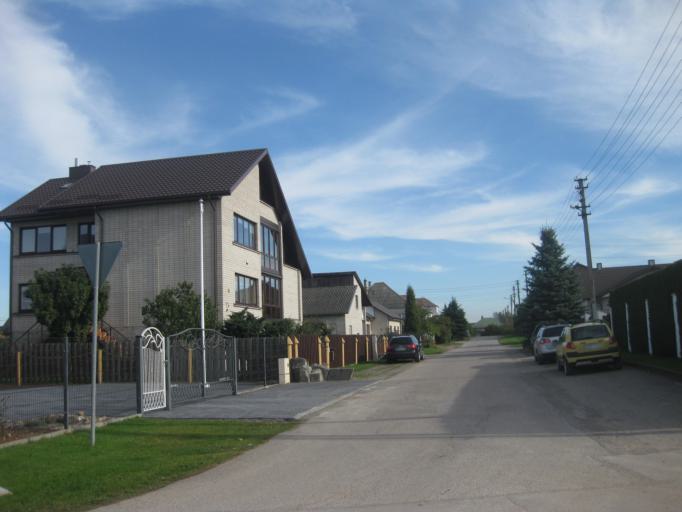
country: LT
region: Kauno apskritis
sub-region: Kauno rajonas
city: Garliava
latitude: 54.8230
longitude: 23.8574
